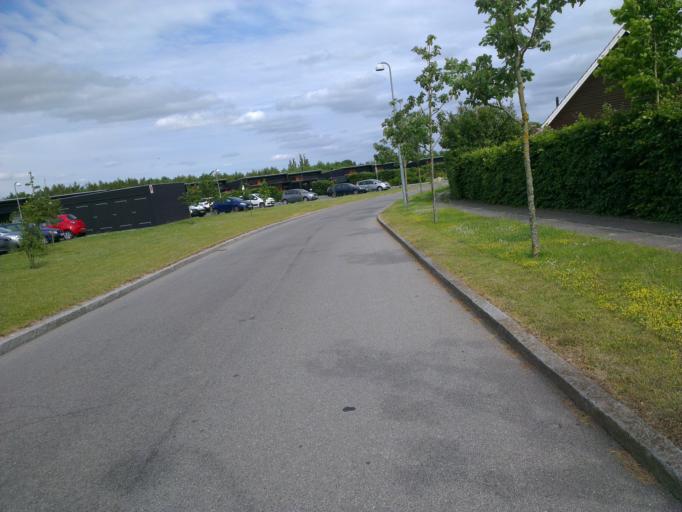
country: DK
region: Capital Region
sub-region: Frederikssund Kommune
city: Frederikssund
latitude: 55.8646
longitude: 12.0773
